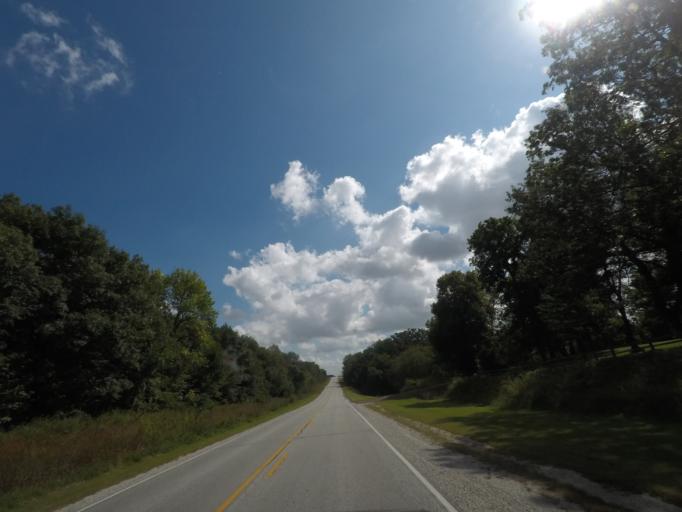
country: US
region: Iowa
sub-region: Story County
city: Nevada
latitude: 42.0227
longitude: -93.3791
